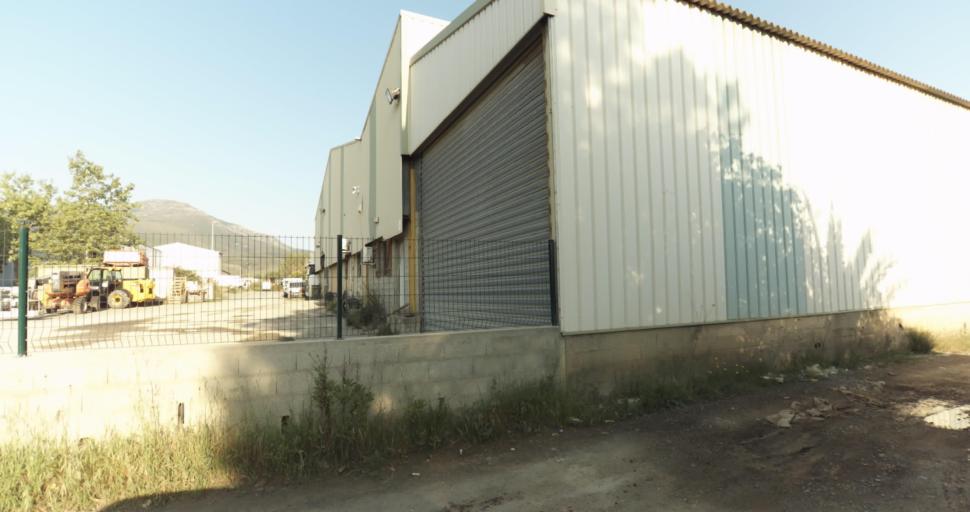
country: FR
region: Corsica
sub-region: Departement de la Haute-Corse
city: Biguglia
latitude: 42.6013
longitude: 9.4460
